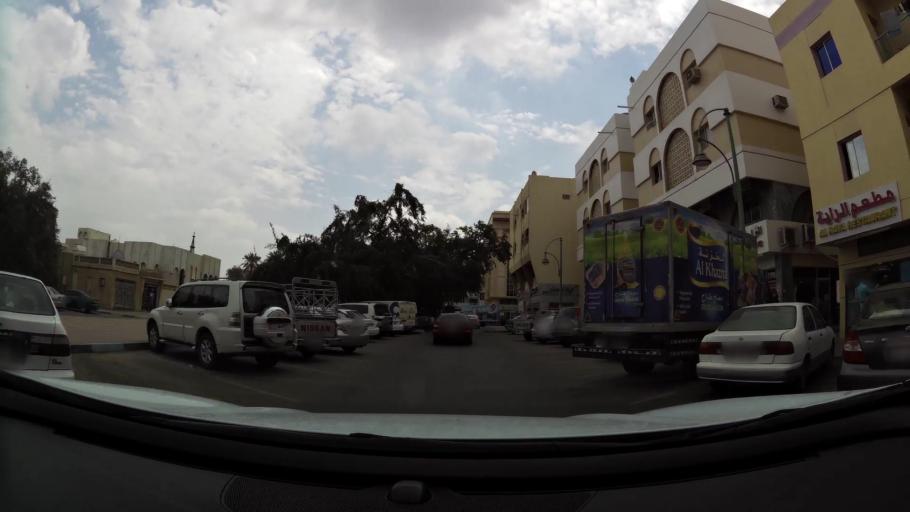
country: AE
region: Abu Dhabi
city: Al Ain
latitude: 24.2177
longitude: 55.7768
